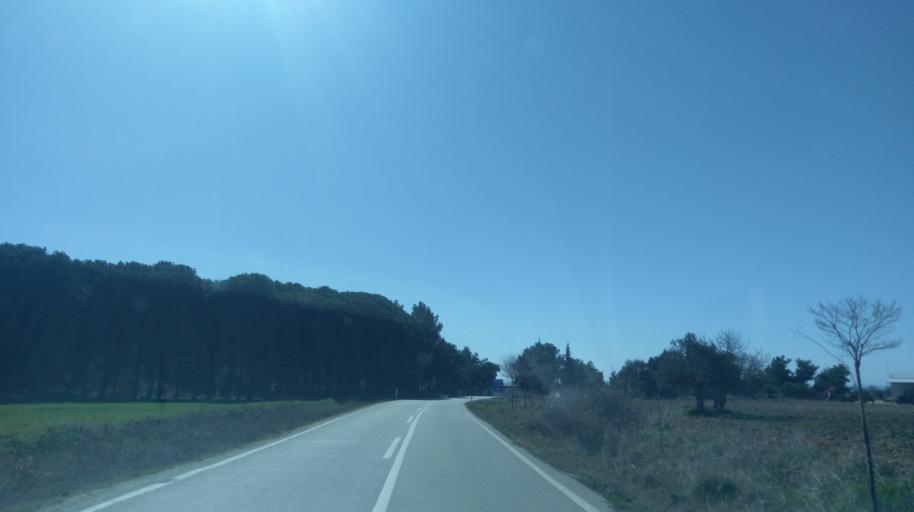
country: TR
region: Canakkale
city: Intepe
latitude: 40.1000
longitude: 26.2285
